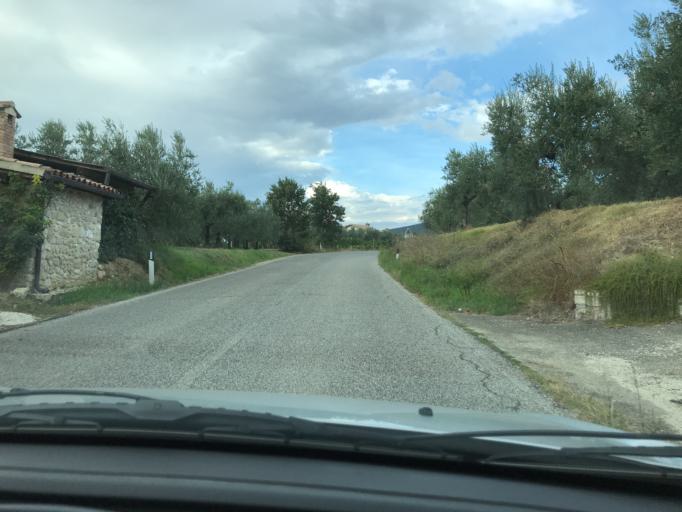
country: IT
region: Umbria
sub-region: Provincia di Terni
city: Montecchio
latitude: 42.6573
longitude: 12.2781
